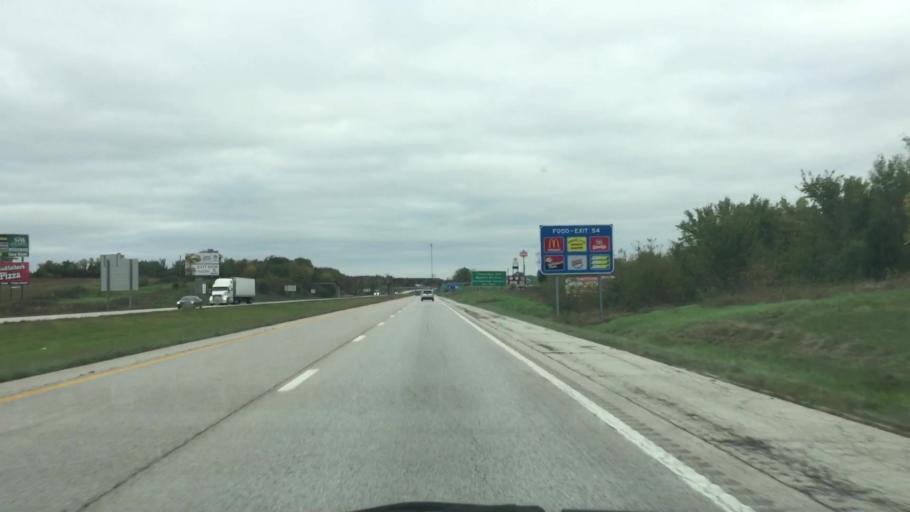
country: US
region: Missouri
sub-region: Clinton County
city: Cameron
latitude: 39.7433
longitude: -94.2200
